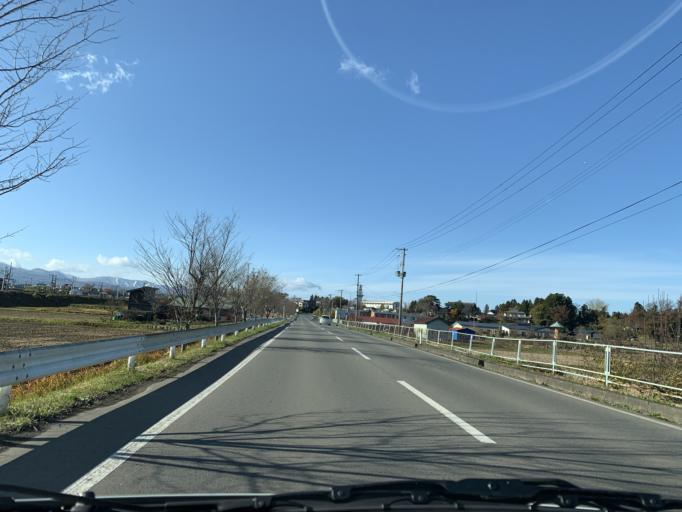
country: JP
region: Iwate
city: Mizusawa
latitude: 39.1913
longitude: 141.1231
